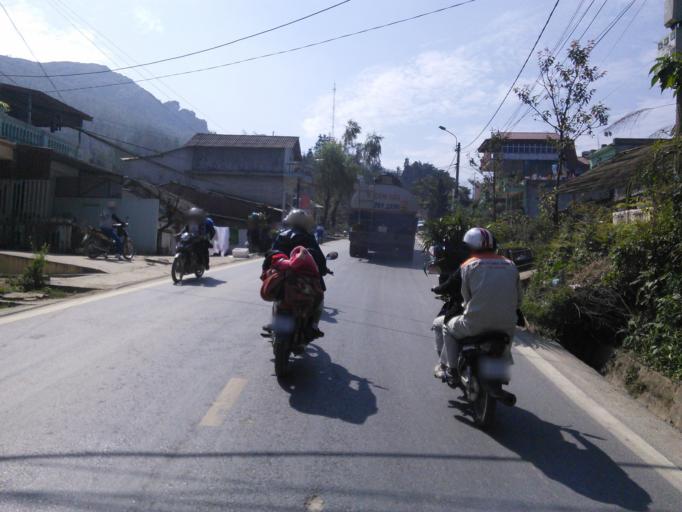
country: VN
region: Lao Cai
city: Sa Pa
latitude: 22.3436
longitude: 103.8575
